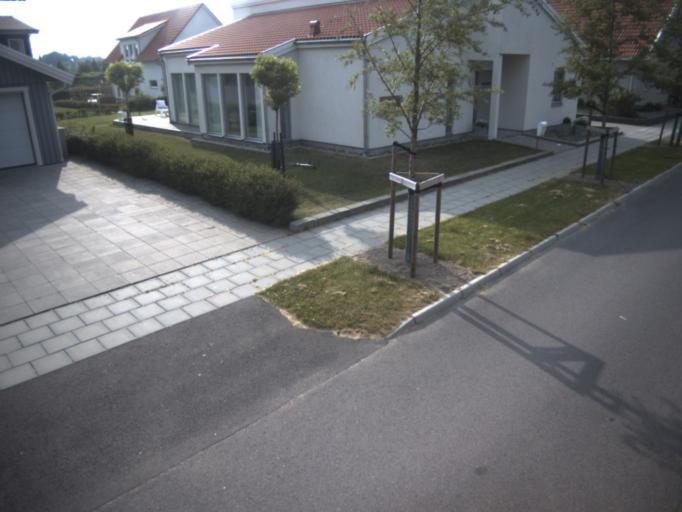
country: SE
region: Skane
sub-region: Helsingborg
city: Helsingborg
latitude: 56.0820
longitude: 12.6996
